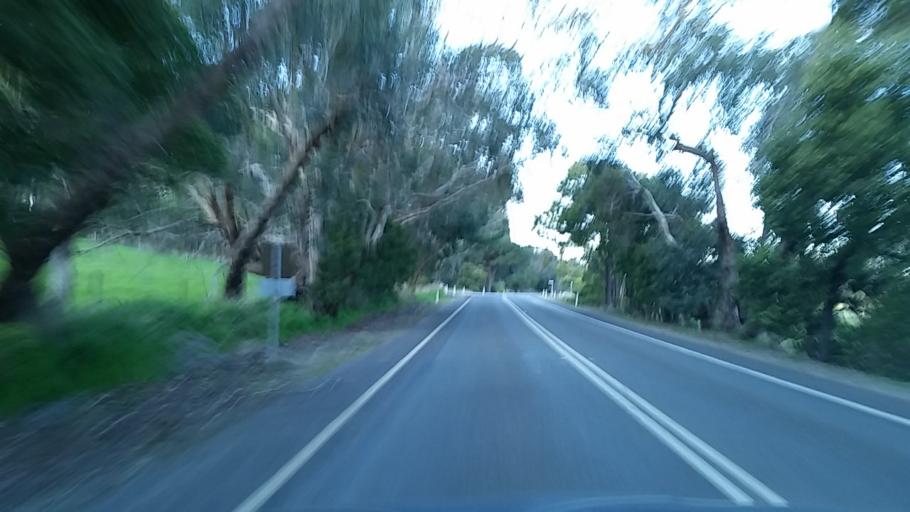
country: AU
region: South Australia
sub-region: Alexandrina
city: Mount Compass
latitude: -35.3163
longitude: 138.5677
